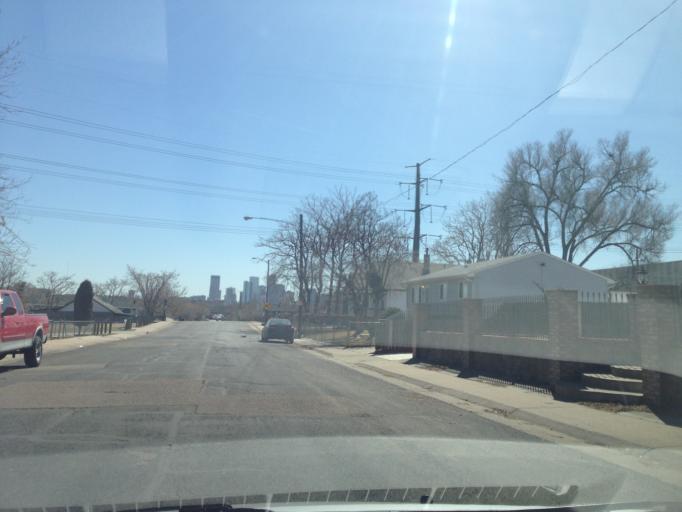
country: US
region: Colorado
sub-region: Adams County
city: Twin Lakes
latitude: 39.7851
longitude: -104.9859
